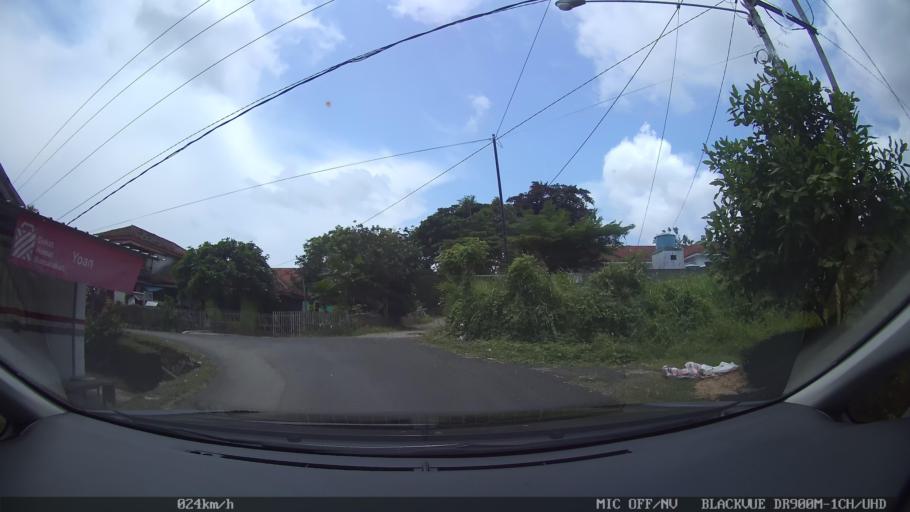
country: ID
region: Lampung
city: Bandarlampung
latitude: -5.4223
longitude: 105.2312
